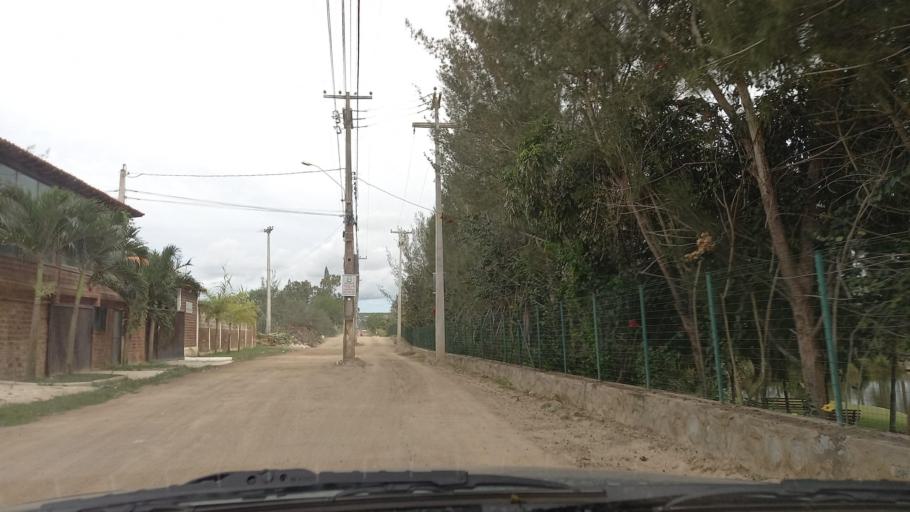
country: BR
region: Pernambuco
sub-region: Gravata
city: Gravata
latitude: -8.1964
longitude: -35.6003
